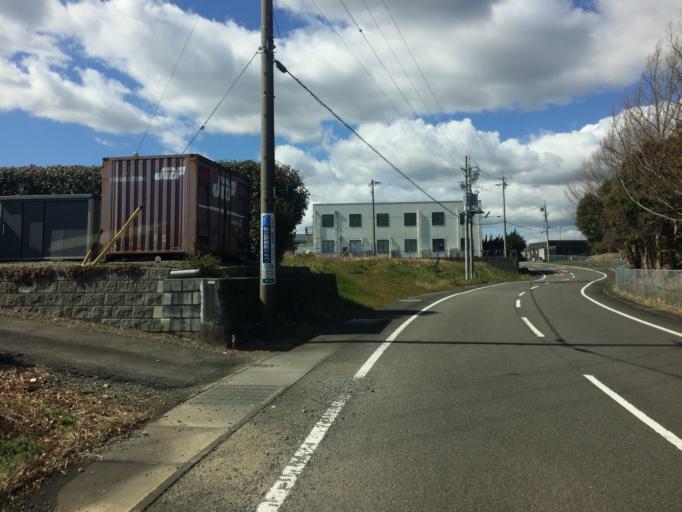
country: JP
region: Shizuoka
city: Shimada
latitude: 34.7576
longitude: 138.1624
